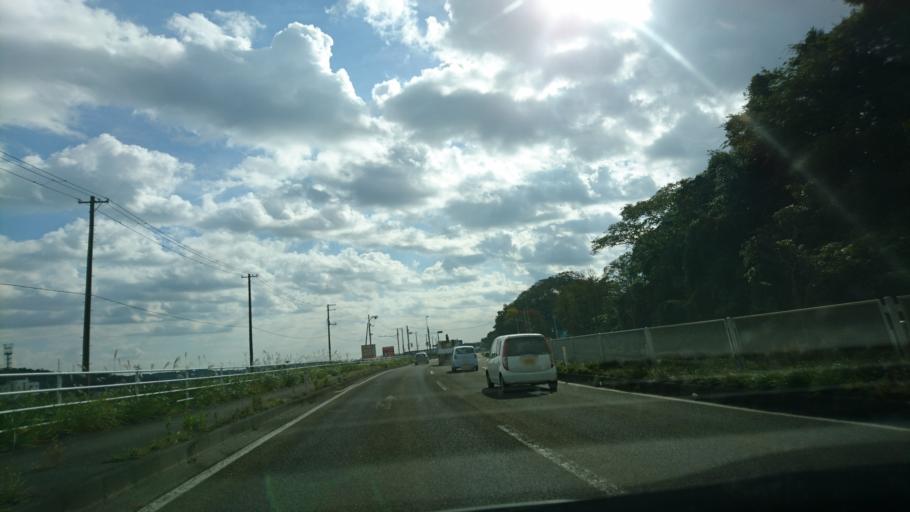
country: JP
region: Miyagi
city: Tomiya
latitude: 38.4519
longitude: 140.8837
